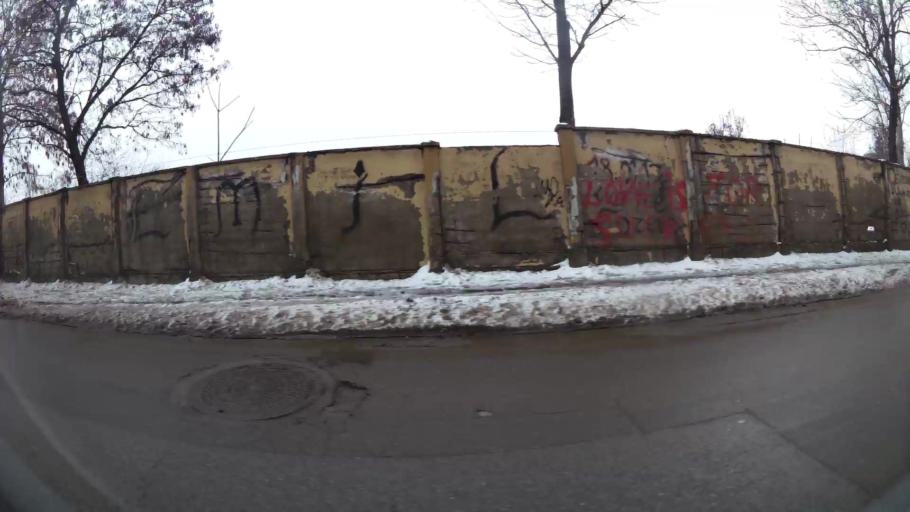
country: BG
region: Sofia-Capital
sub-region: Stolichna Obshtina
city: Sofia
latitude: 42.7120
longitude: 23.3376
